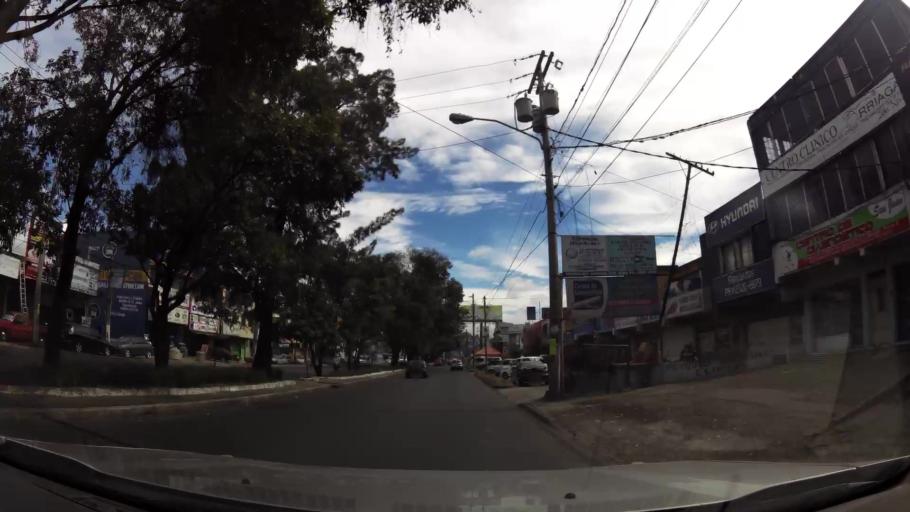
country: GT
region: Guatemala
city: Mixco
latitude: 14.6434
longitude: -90.5733
